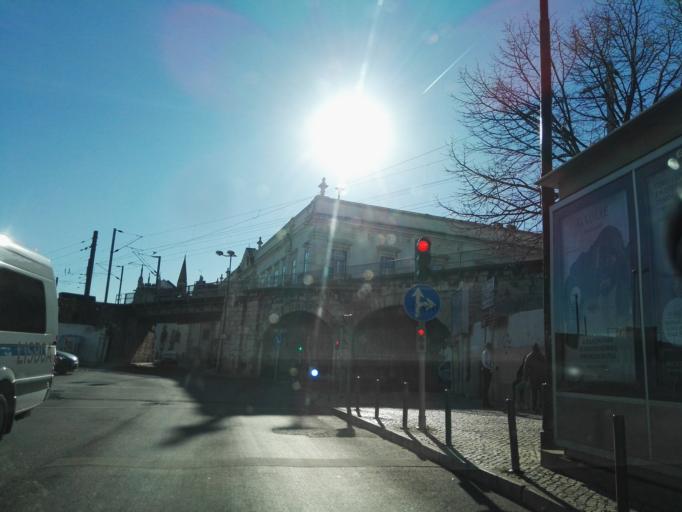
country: PT
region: Lisbon
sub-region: Lisbon
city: Lisbon
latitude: 38.7259
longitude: -9.1126
